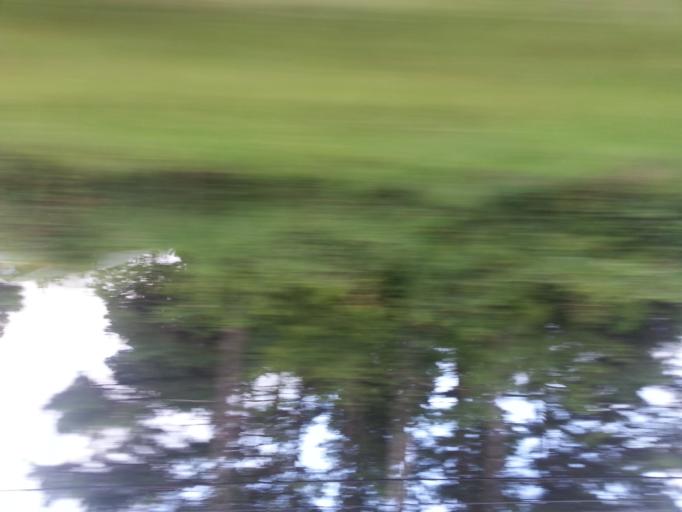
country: US
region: Alabama
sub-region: Madison County
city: Madison
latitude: 34.7535
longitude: -86.7089
